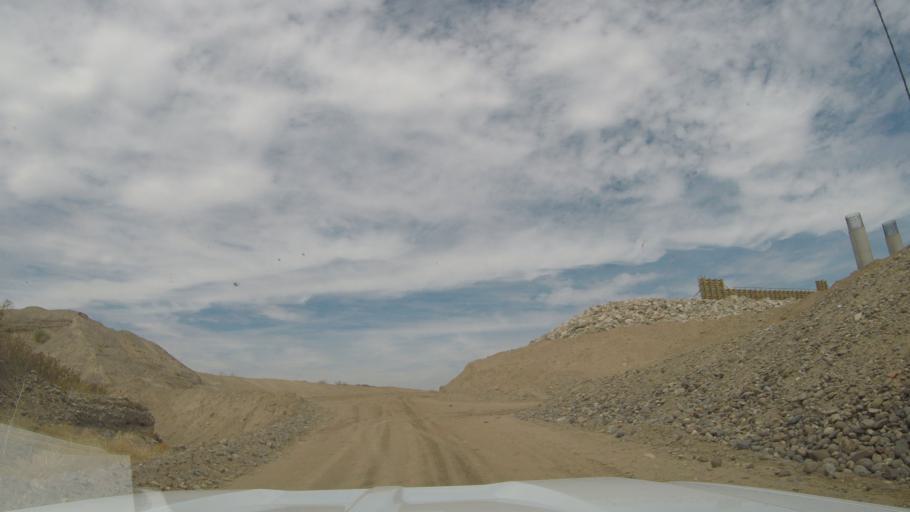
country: US
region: Arizona
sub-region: Maricopa County
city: Laveen
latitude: 33.4021
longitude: -112.1927
